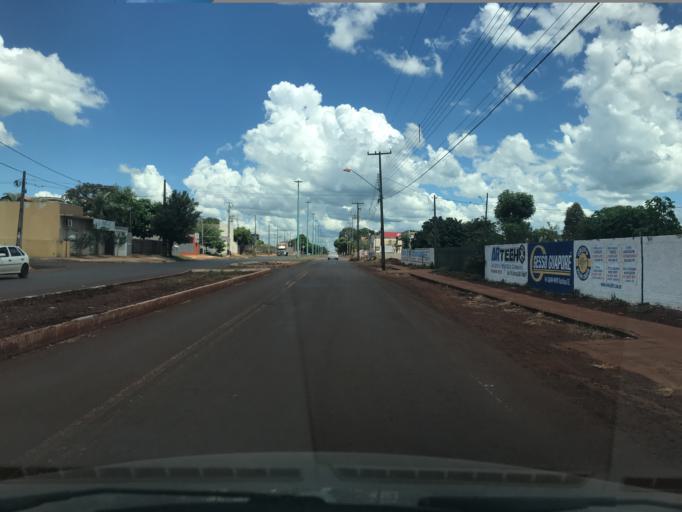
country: BR
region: Parana
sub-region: Palotina
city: Palotina
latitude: -24.2692
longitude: -53.8417
